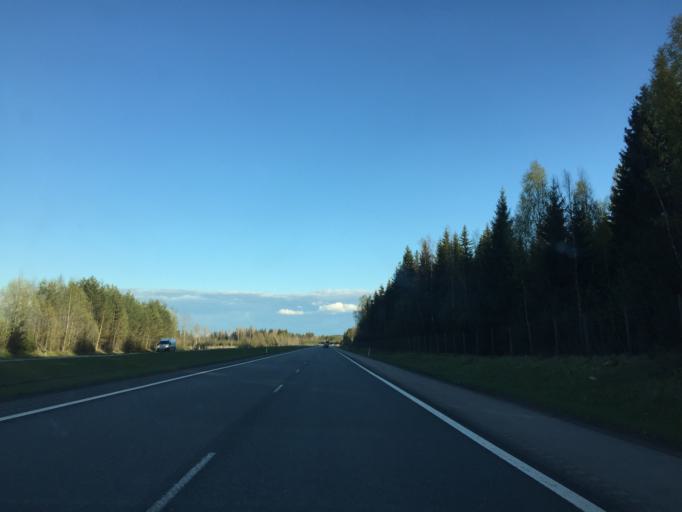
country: FI
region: Haeme
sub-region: Haemeenlinna
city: Tervakoski
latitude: 60.7881
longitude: 24.6989
